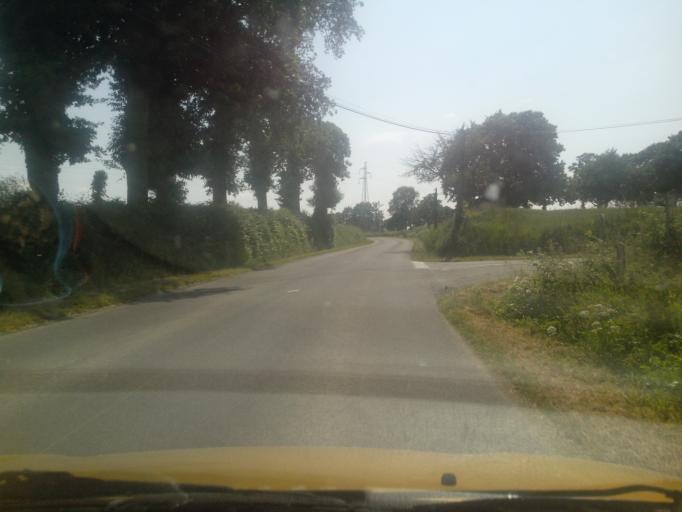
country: FR
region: Brittany
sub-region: Departement d'Ille-et-Vilaine
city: Melesse
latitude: 48.2350
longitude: -1.6791
